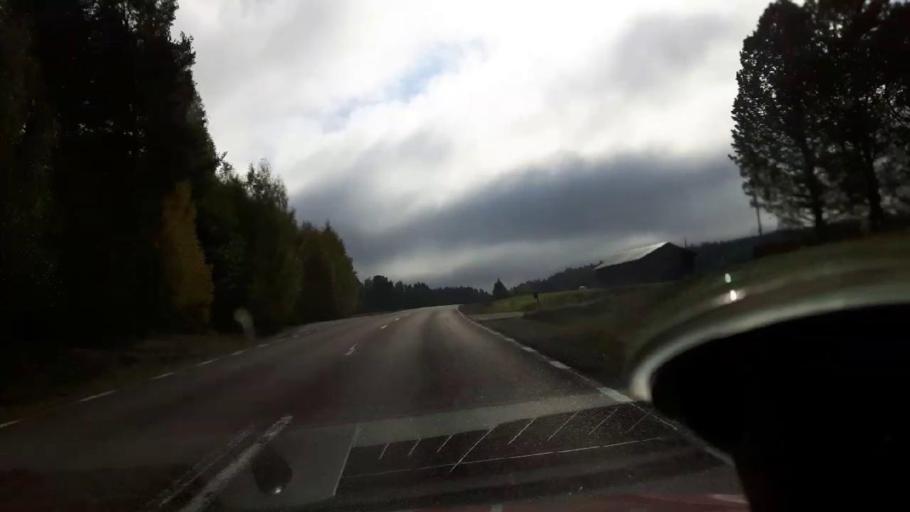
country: SE
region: Gaevleborg
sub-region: Ljusdals Kommun
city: Farila
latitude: 61.8775
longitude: 15.7171
